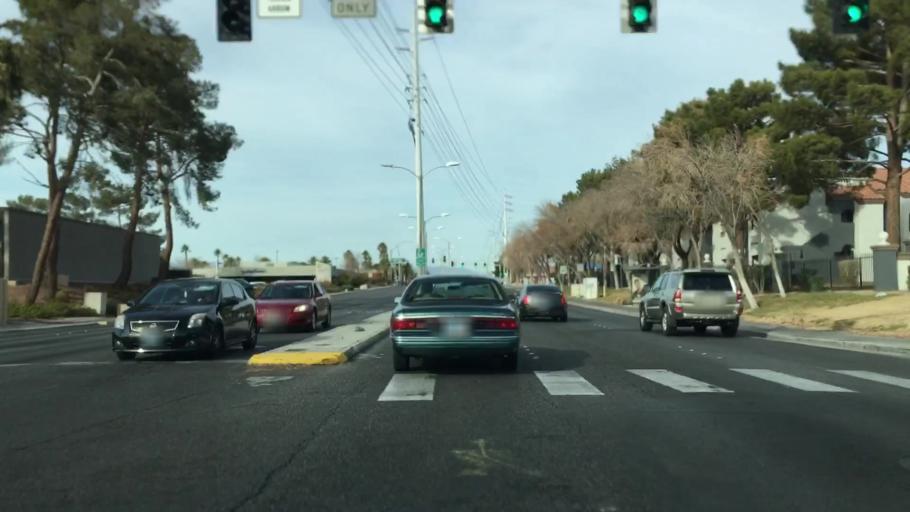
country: US
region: Nevada
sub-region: Clark County
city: Whitney
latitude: 36.0671
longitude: -115.0824
